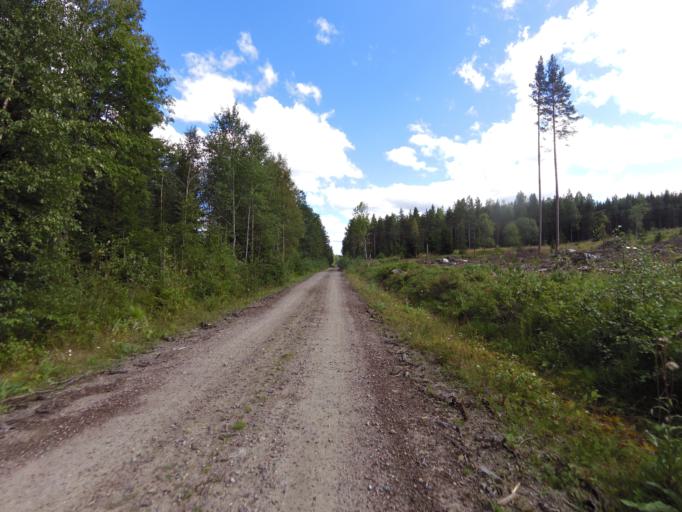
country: SE
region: Gaevleborg
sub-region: Hofors Kommun
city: Hofors
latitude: 60.5217
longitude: 16.2509
